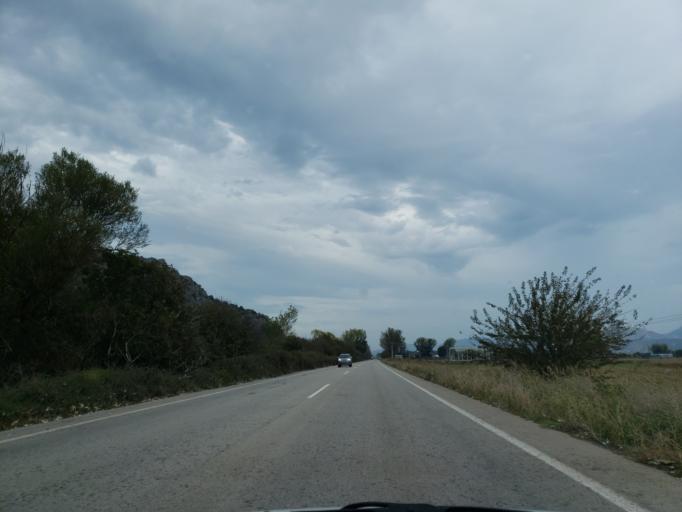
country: GR
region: Central Greece
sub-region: Nomos Voiotias
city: Akraifnia
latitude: 38.4764
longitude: 23.1188
